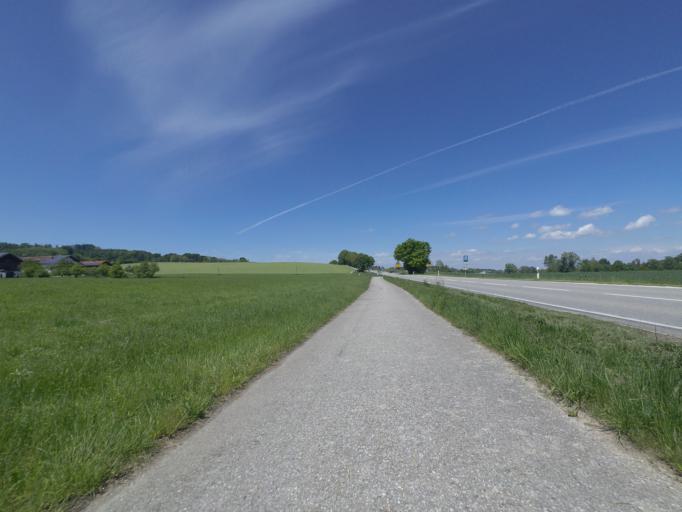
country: DE
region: Bavaria
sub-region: Upper Bavaria
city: Taching am See
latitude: 47.9520
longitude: 12.7339
